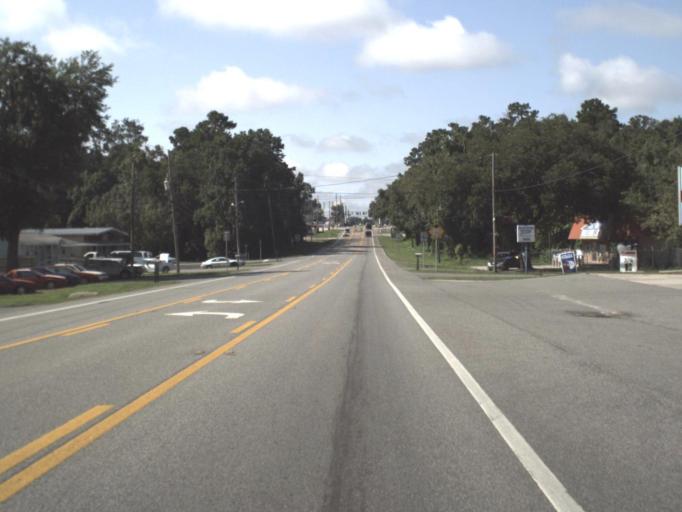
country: US
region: Florida
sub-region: Hernando County
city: Brooksville
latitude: 28.5598
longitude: -82.3977
